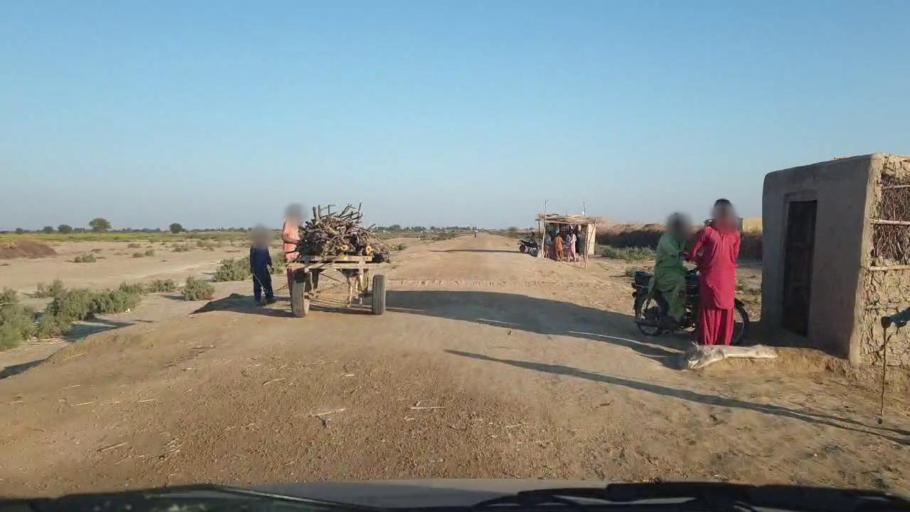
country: PK
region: Sindh
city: Samaro
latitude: 25.3216
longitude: 69.2919
